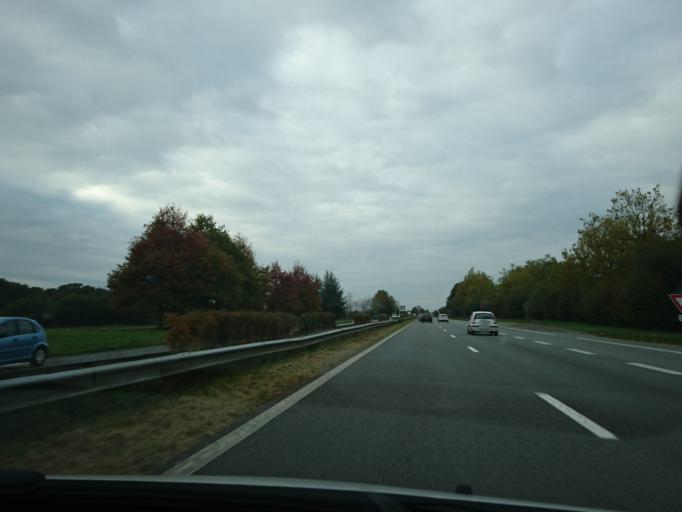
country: FR
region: Pays de la Loire
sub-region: Departement de la Loire-Atlantique
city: Missillac
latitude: 47.4522
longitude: -2.1334
